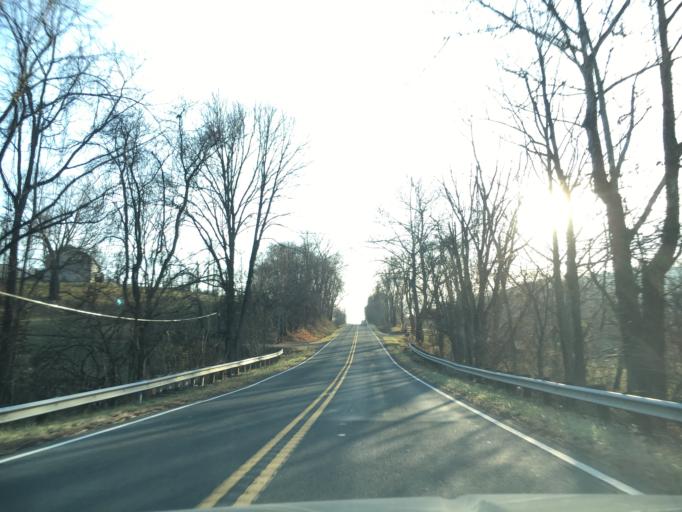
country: US
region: Virginia
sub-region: Rappahannock County
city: Washington
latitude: 38.7560
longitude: -78.1013
